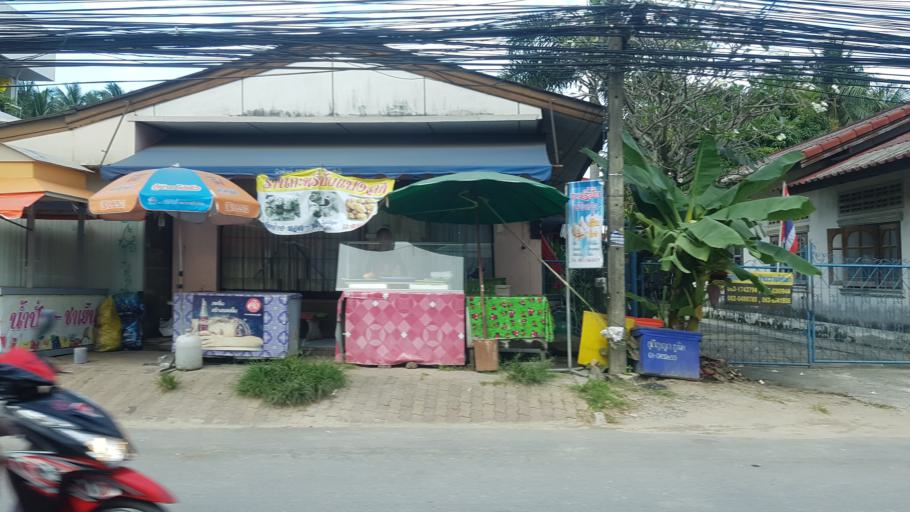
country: TH
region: Surat Thani
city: Ko Samui
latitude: 9.5252
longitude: 100.0468
